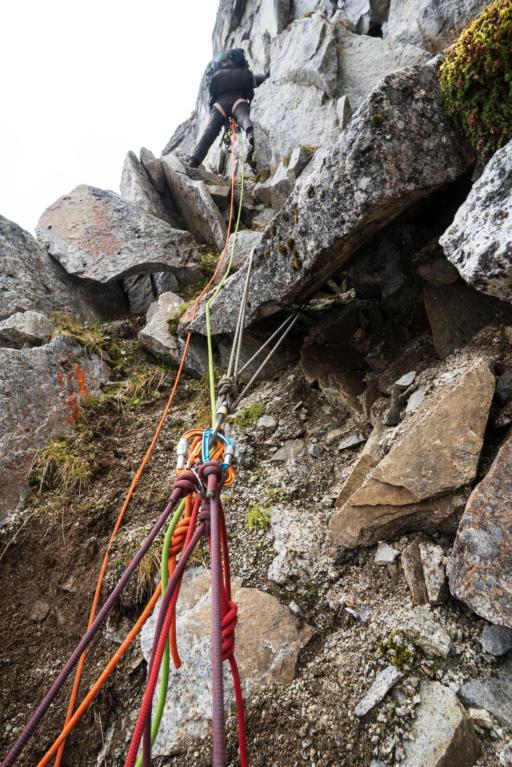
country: RU
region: Transbaikal Territory
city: Chara
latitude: 56.8706
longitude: 117.5669
